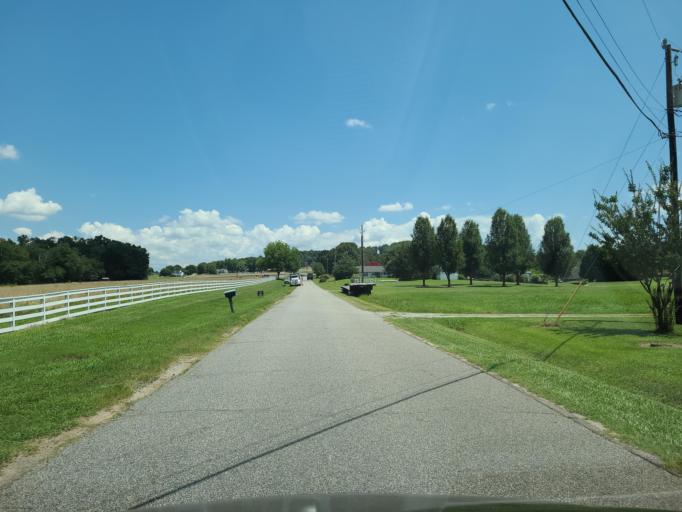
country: US
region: South Carolina
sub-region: Spartanburg County
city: Inman Mills
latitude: 35.0400
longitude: -82.1578
